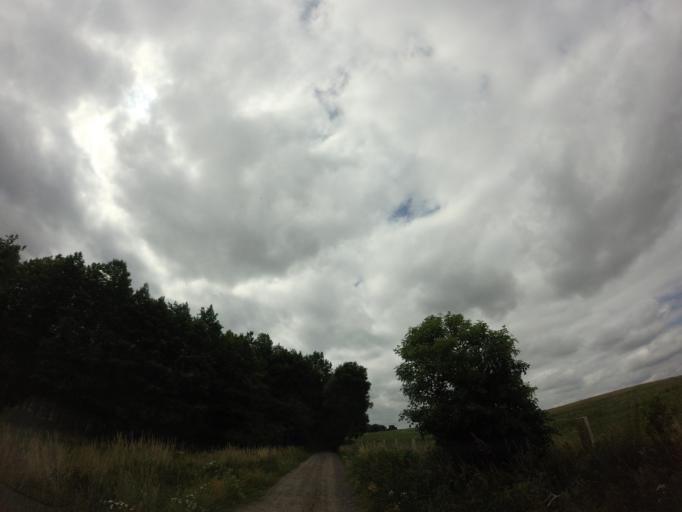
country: PL
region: West Pomeranian Voivodeship
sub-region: Powiat choszczenski
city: Bierzwnik
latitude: 52.9519
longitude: 15.6104
